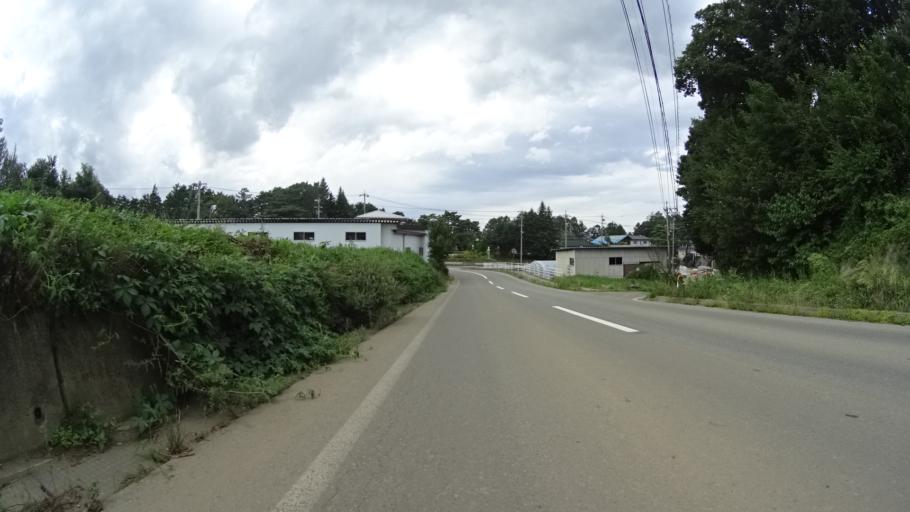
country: JP
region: Nagano
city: Saku
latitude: 35.9985
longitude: 138.5006
